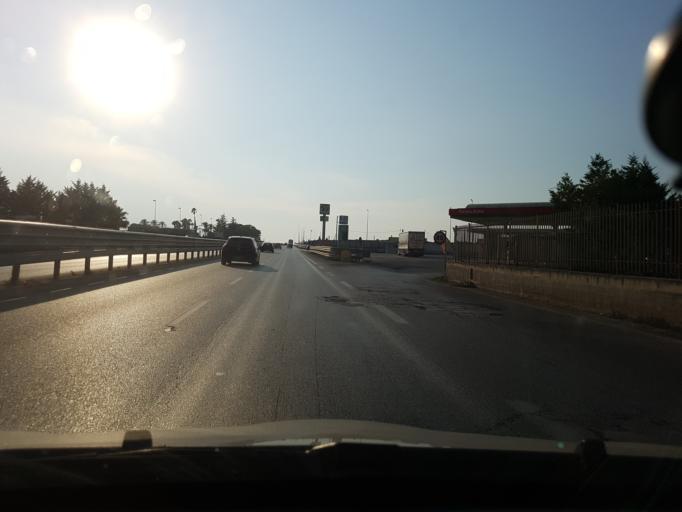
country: IT
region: Apulia
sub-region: Provincia di Foggia
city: Cerignola
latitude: 41.2775
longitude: 15.8640
